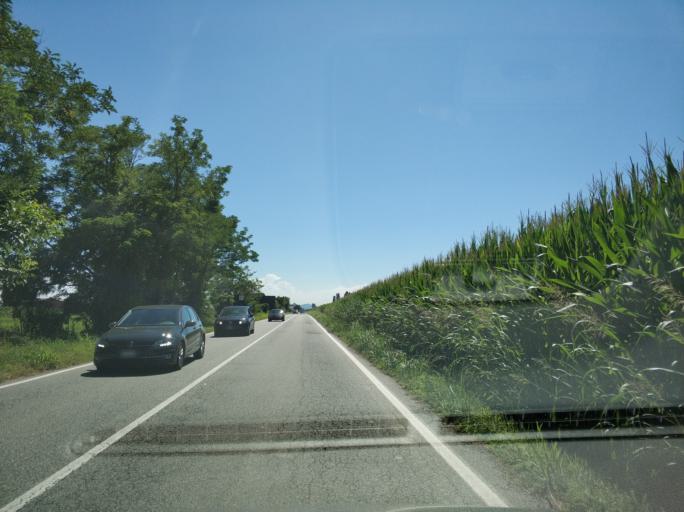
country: IT
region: Piedmont
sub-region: Provincia di Vercelli
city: Cigliano
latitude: 45.2970
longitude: 8.0049
